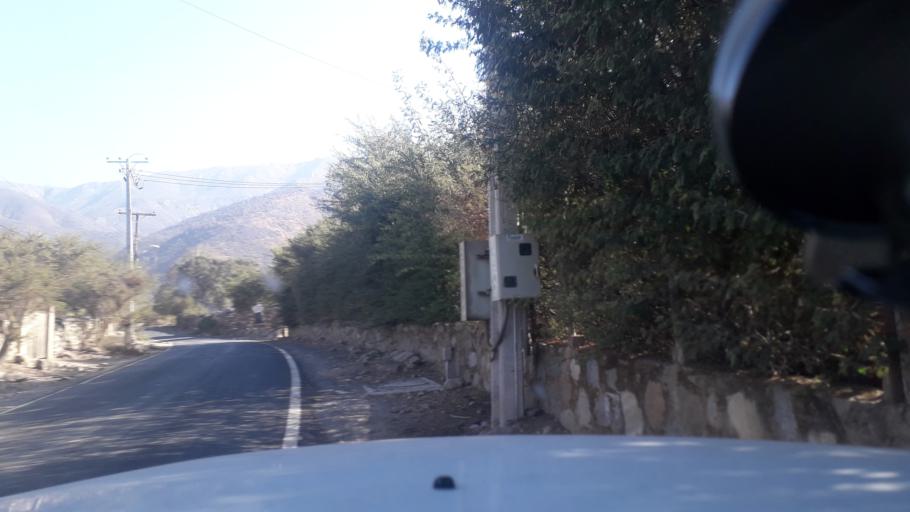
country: CL
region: Valparaiso
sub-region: Provincia de Marga Marga
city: Limache
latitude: -33.0583
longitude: -71.1148
